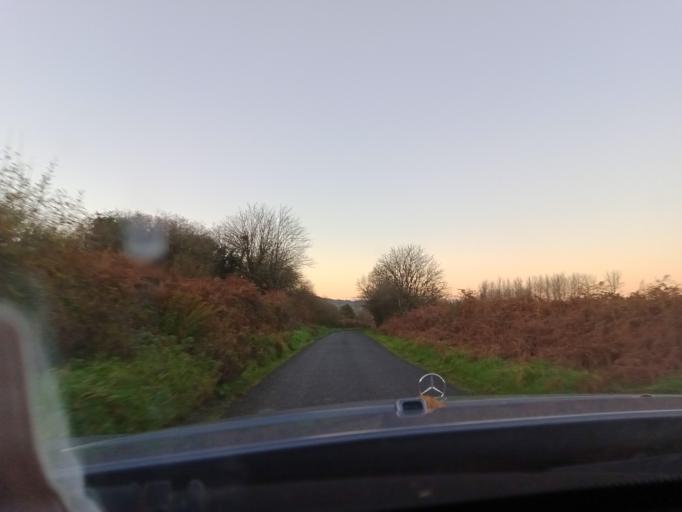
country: IE
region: Leinster
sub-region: Kilkenny
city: Thomastown
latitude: 52.4329
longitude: -7.1048
